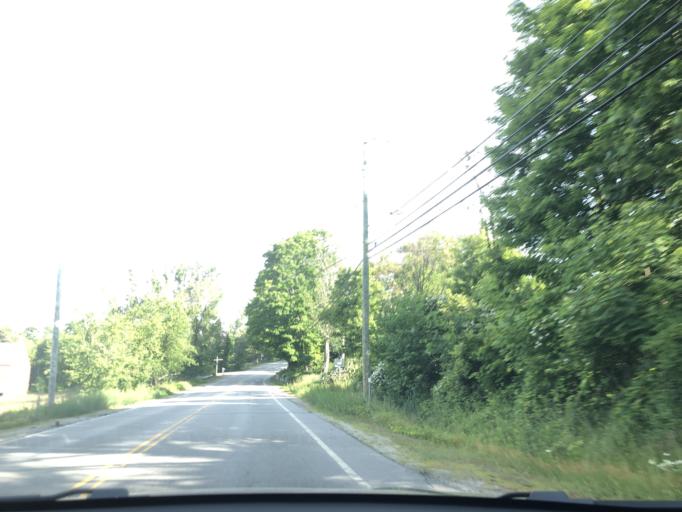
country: US
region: New Hampshire
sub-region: Merrimack County
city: New London
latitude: 43.4024
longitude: -71.9670
